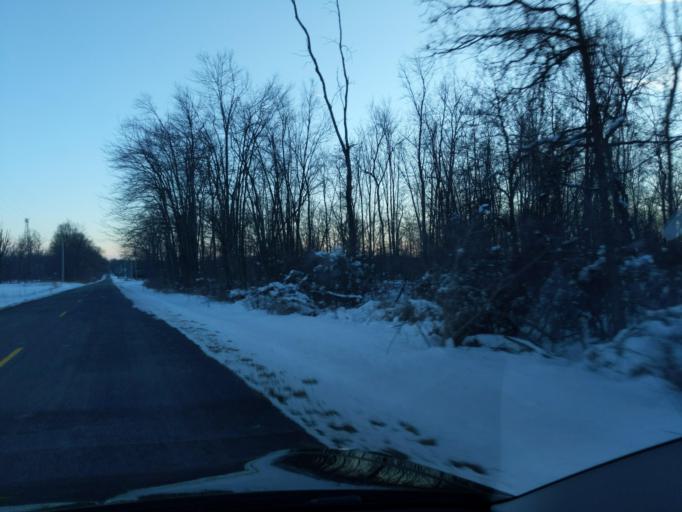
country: US
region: Michigan
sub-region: Ingham County
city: Williamston
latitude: 42.5716
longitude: -84.3180
